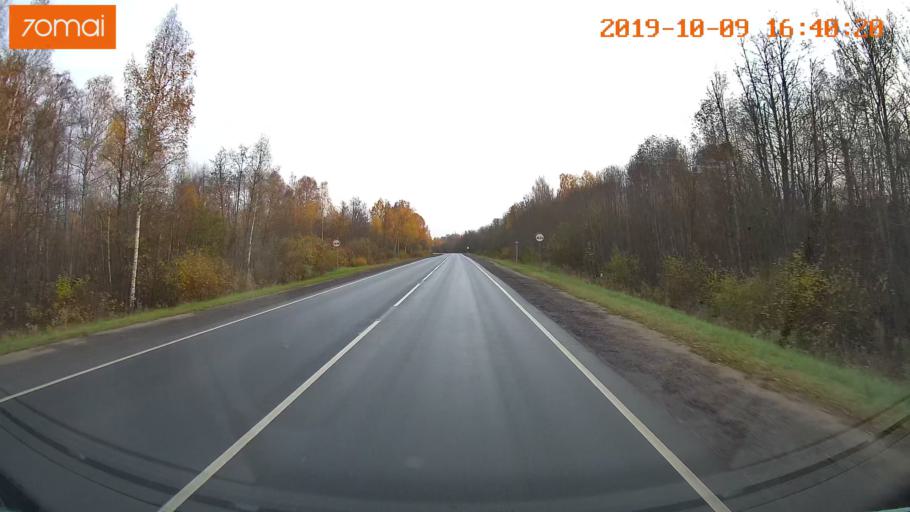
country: RU
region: Kostroma
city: Volgorechensk
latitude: 57.4850
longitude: 41.0595
